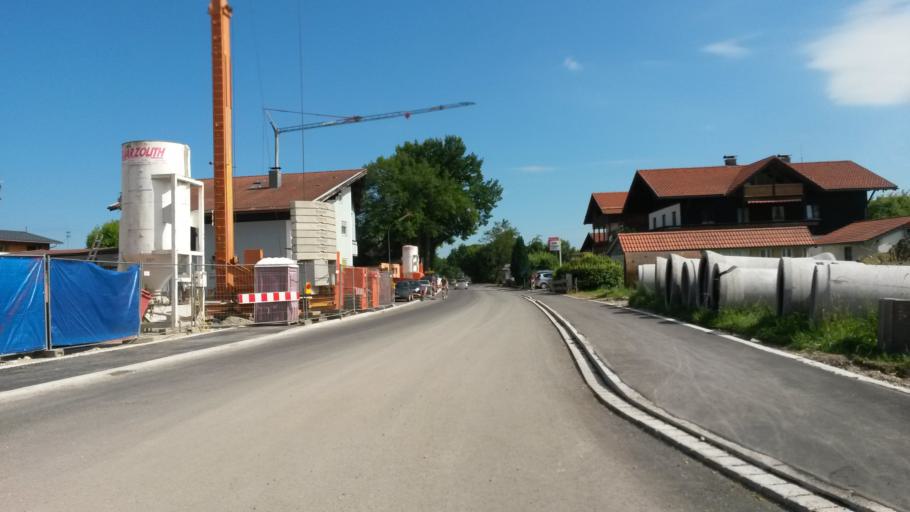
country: DE
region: Bavaria
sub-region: Upper Bavaria
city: Ubersee
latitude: 47.8340
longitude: 12.4881
